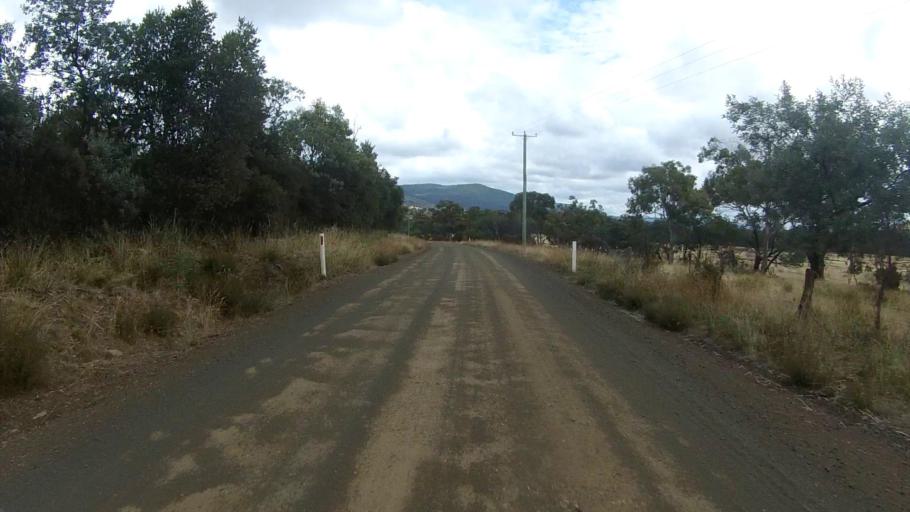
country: AU
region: Tasmania
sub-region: Break O'Day
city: St Helens
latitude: -41.8223
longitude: 147.9882
